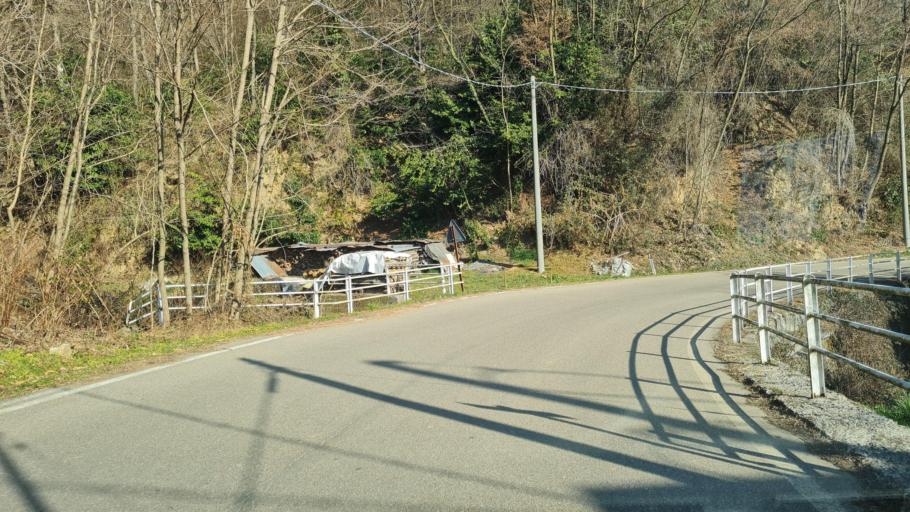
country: IT
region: Piedmont
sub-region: Provincia di Biella
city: Livera
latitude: 45.6132
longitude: 8.1168
